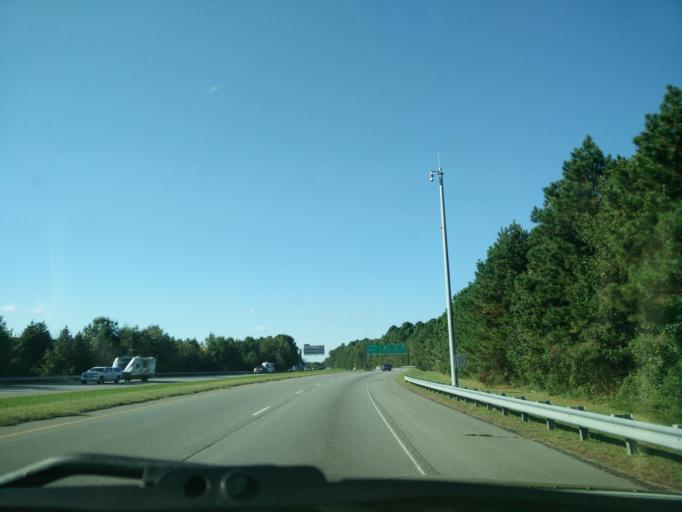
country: US
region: Virginia
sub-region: City of Chesapeake
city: Chesapeake
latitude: 36.7464
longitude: -76.2580
